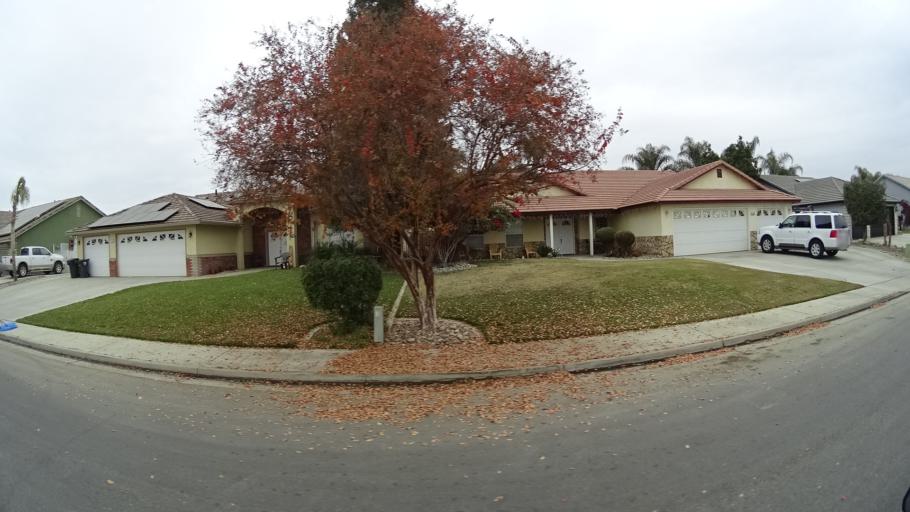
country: US
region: California
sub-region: Kern County
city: Greenfield
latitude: 35.2897
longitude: -119.0369
